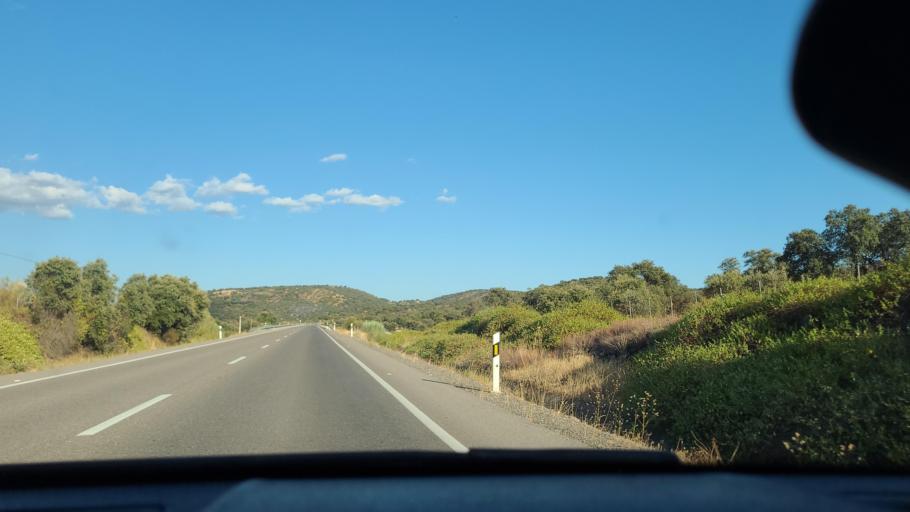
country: ES
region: Andalusia
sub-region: Province of Cordoba
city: Espiel
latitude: 38.2035
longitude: -5.1139
